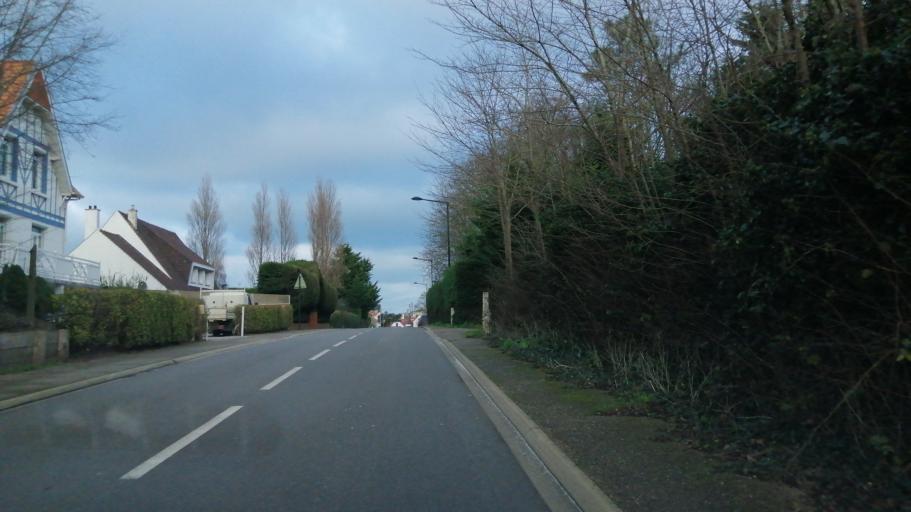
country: FR
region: Nord-Pas-de-Calais
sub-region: Departement du Pas-de-Calais
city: Wissant
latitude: 50.8811
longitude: 1.6584
